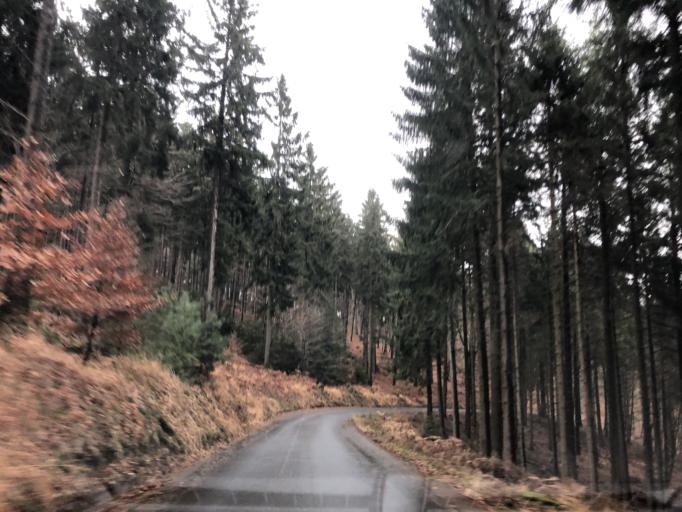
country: DE
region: Baden-Wuerttemberg
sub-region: Karlsruhe Region
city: Dossenheim
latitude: 49.4541
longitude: 8.7097
